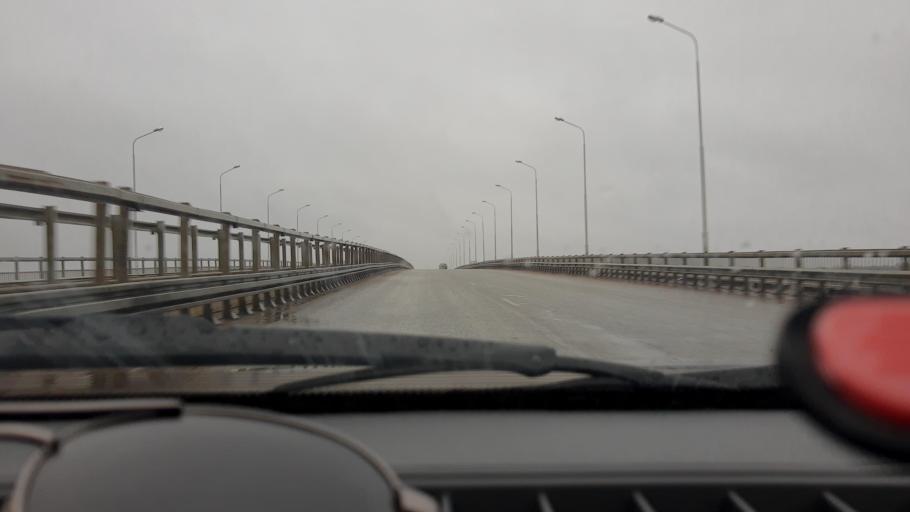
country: RU
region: Bashkortostan
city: Ufa
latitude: 54.6847
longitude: 55.9965
